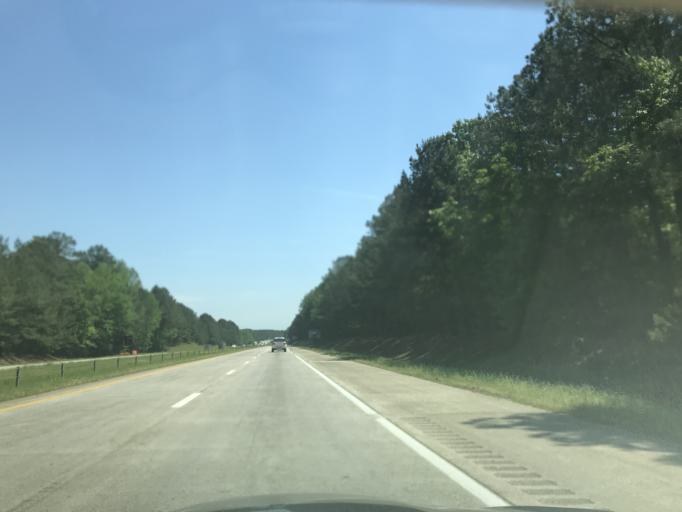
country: US
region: North Carolina
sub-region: Johnston County
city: Benson
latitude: 35.5273
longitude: -78.5657
